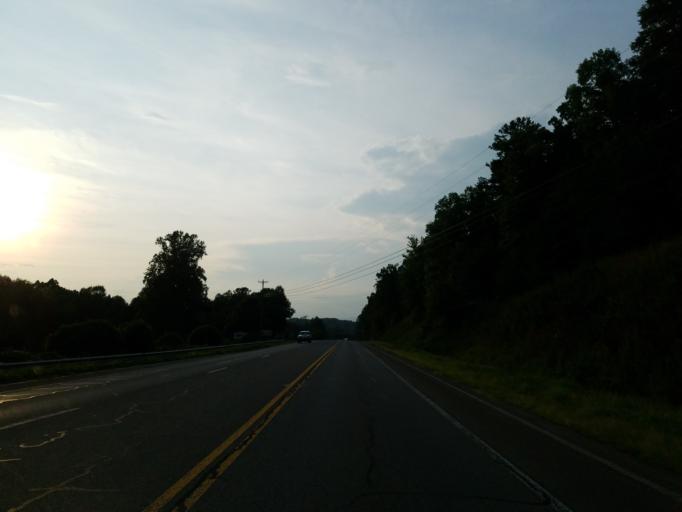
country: US
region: Georgia
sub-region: Gilmer County
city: Ellijay
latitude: 34.6646
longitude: -84.4501
